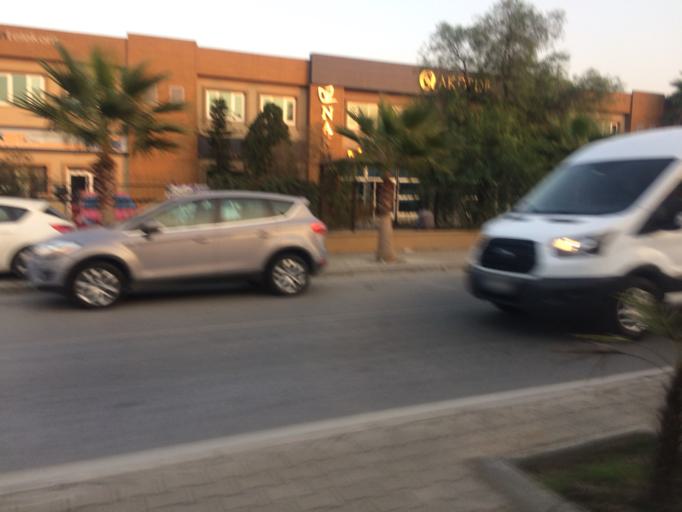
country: TR
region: Izmir
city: Karsiyaka
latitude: 38.4992
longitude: 27.0371
